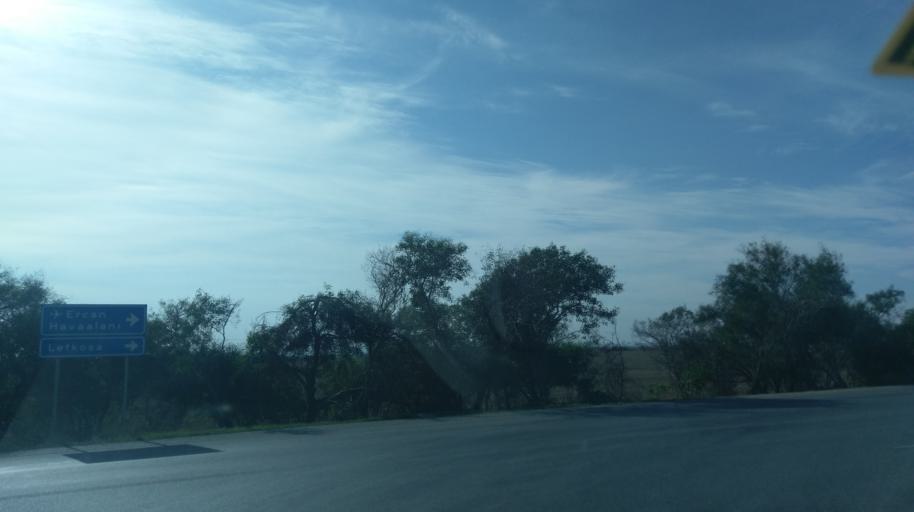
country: CY
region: Ammochostos
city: Acheritou
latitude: 35.1531
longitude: 33.8461
